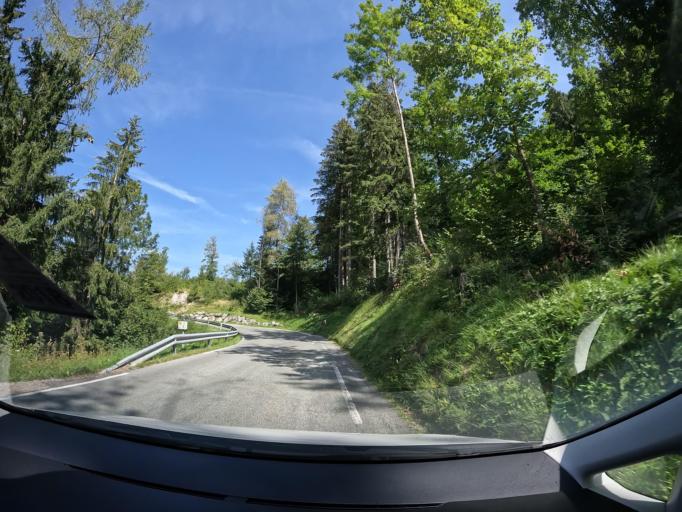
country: AT
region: Carinthia
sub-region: Politischer Bezirk Klagenfurt Land
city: Schiefling am See
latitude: 46.5759
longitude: 14.0786
